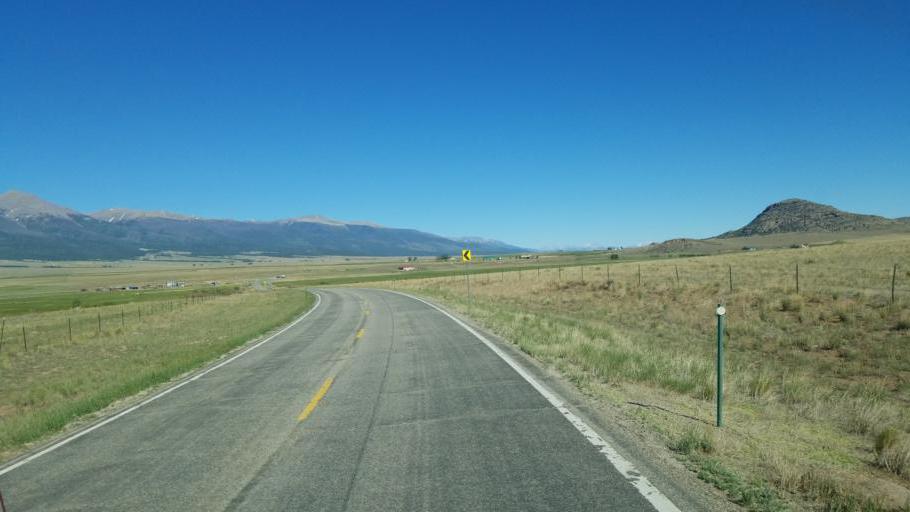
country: US
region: Colorado
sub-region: Custer County
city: Westcliffe
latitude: 38.1680
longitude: -105.4903
